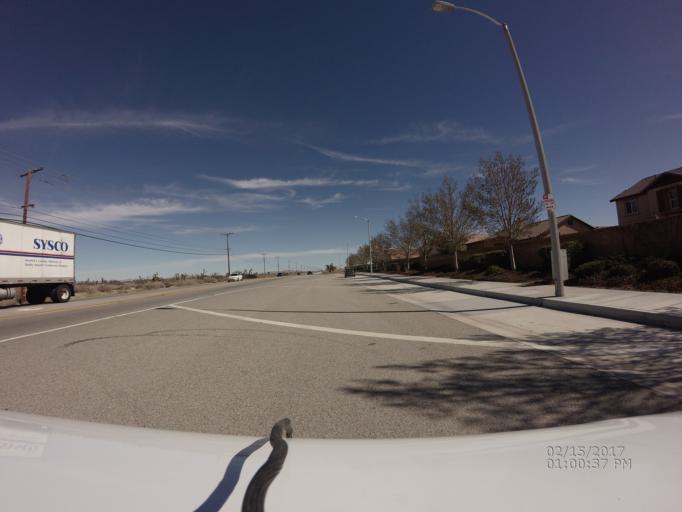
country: US
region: California
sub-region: Los Angeles County
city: Littlerock
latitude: 34.5797
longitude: -118.0245
